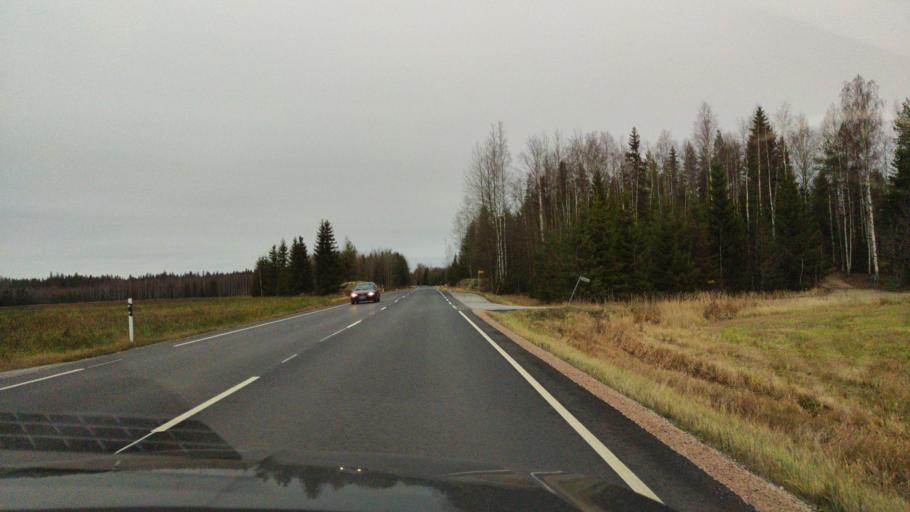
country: FI
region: Varsinais-Suomi
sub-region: Loimaa
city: Aura
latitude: 60.7119
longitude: 22.4437
